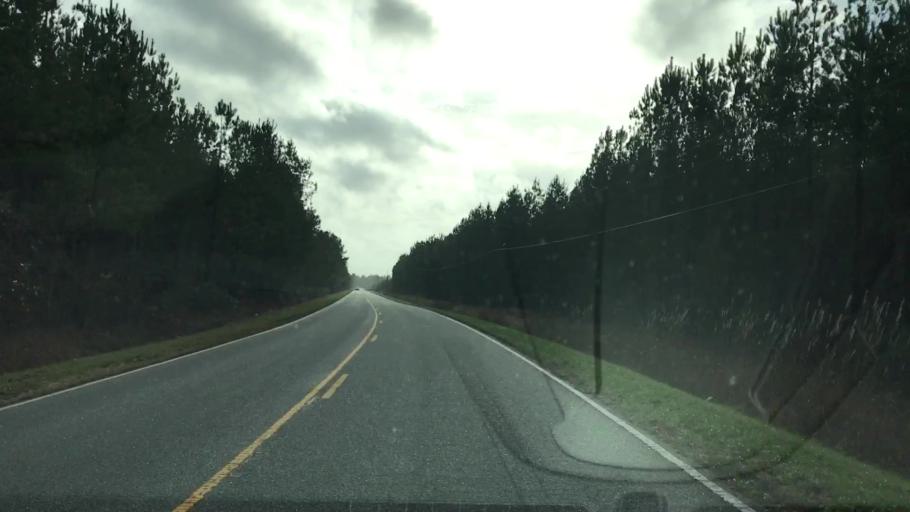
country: US
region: South Carolina
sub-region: Williamsburg County
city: Andrews
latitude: 33.4177
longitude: -79.6031
